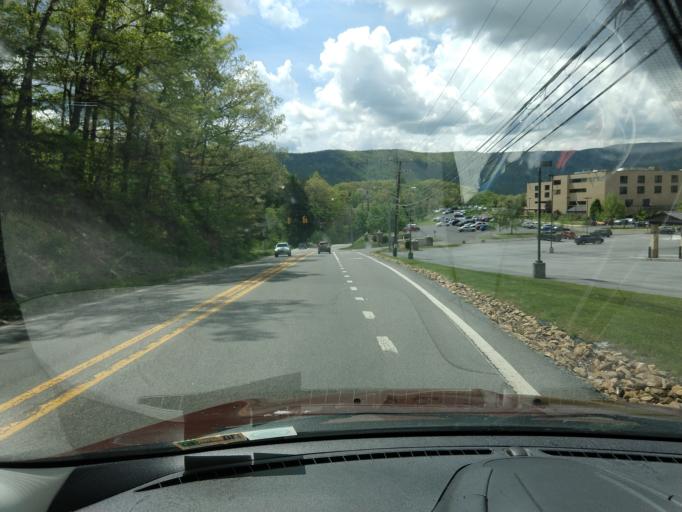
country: US
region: West Virginia
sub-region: Mercer County
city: Bluefield
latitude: 37.2580
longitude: -81.2342
